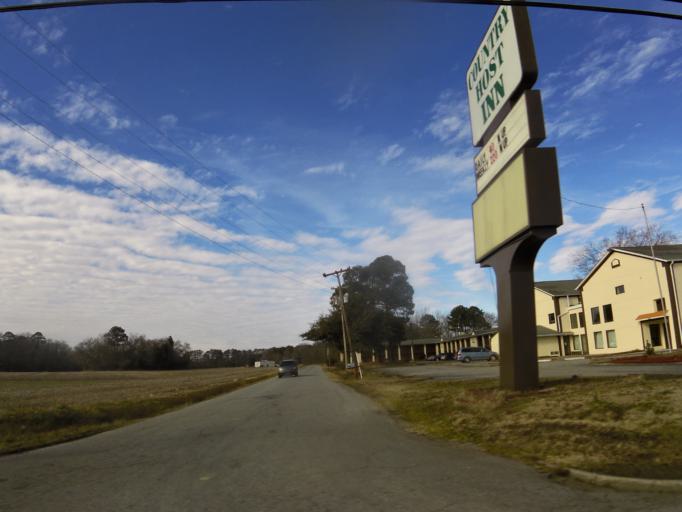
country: US
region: Virginia
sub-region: City of Franklin
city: Franklin
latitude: 36.6893
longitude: -76.9020
